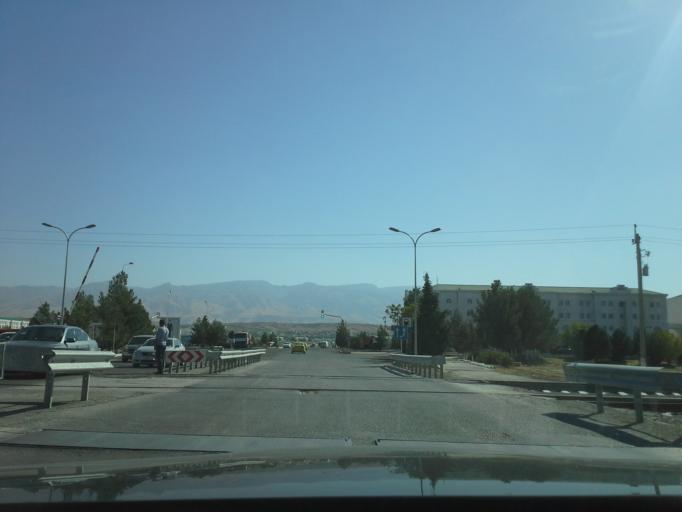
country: TM
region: Ahal
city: Ashgabat
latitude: 37.9875
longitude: 58.3280
